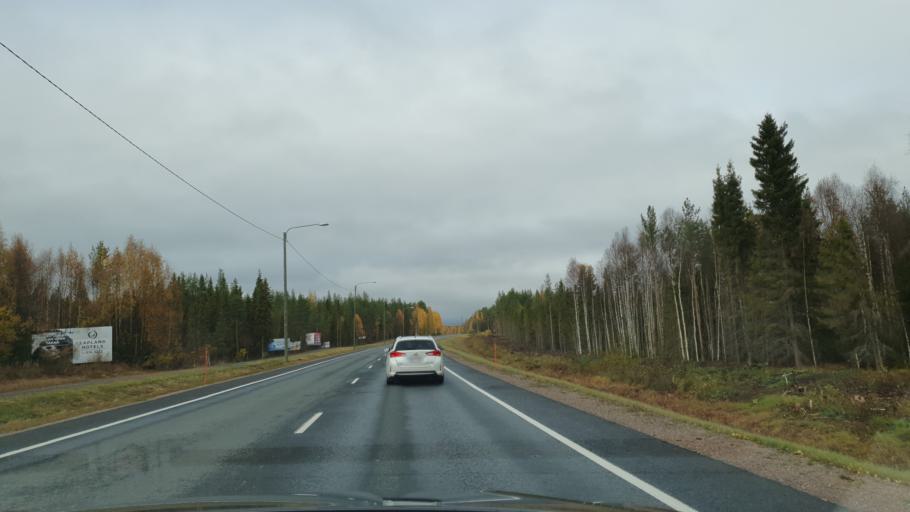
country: FI
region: Lapland
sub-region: Rovaniemi
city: Rovaniemi
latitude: 66.6372
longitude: 25.4960
